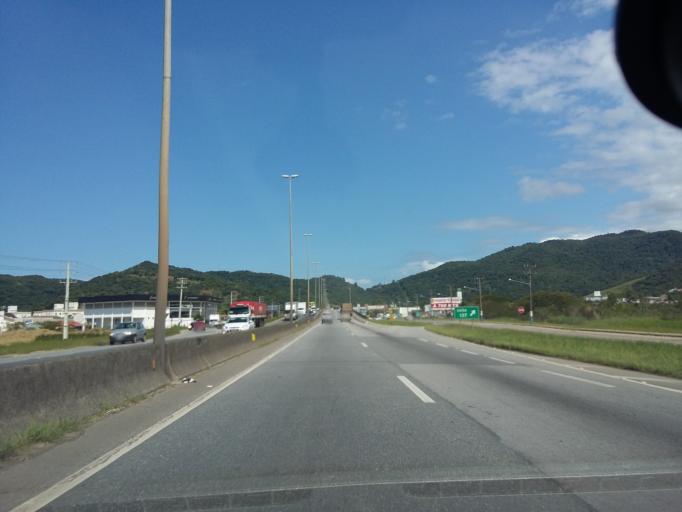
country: BR
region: Santa Catarina
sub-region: Balneario Camboriu
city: Balneario Camboriu
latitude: -27.0161
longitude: -48.6117
